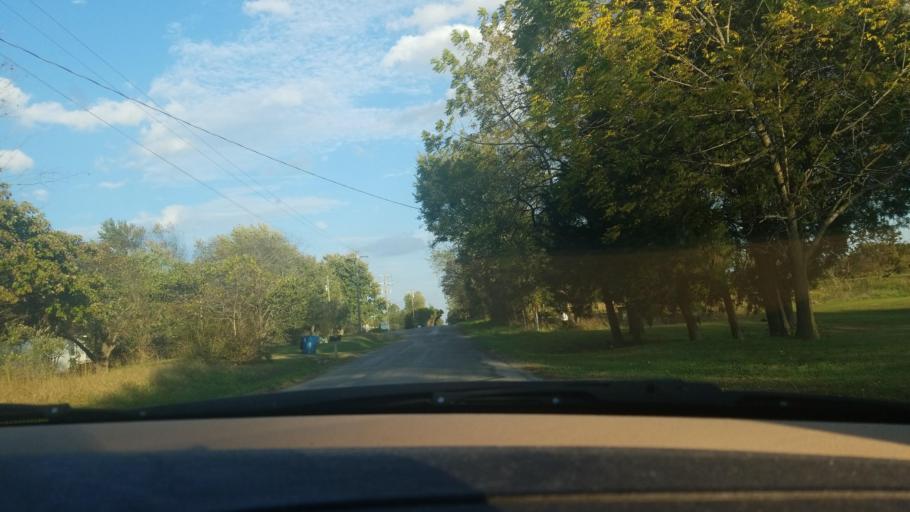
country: US
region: Illinois
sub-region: Saline County
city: Carrier Mills
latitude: 37.7720
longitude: -88.7312
